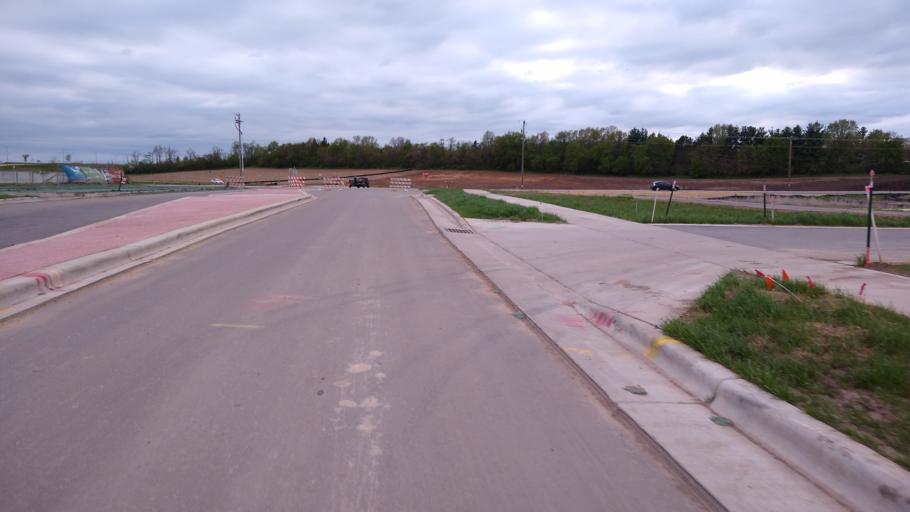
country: US
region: Wisconsin
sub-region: Dane County
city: Monona
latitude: 43.0115
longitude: -89.3745
